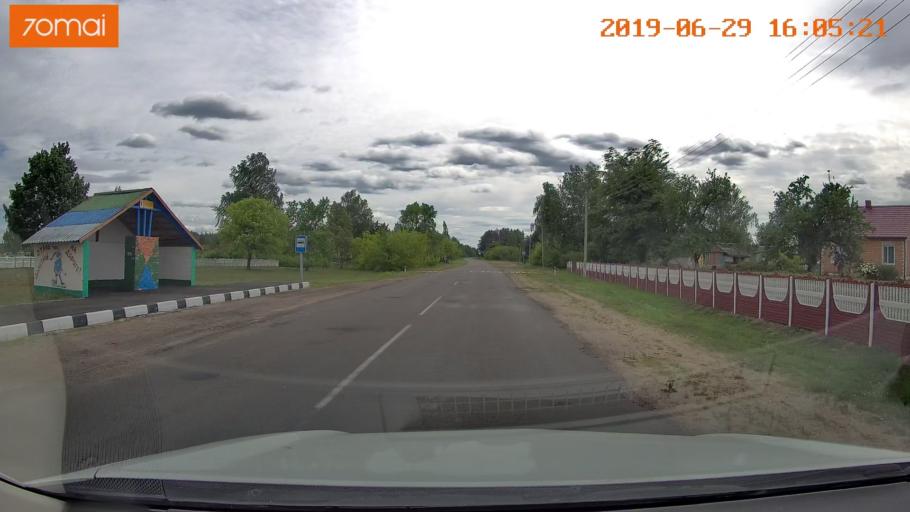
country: BY
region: Brest
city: Luninyets
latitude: 52.2170
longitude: 27.0198
